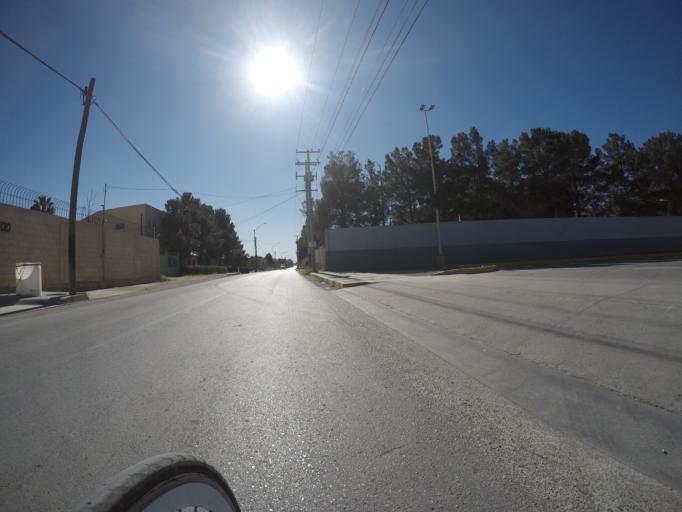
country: US
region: Texas
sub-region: El Paso County
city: Socorro
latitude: 31.6945
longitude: -106.3896
